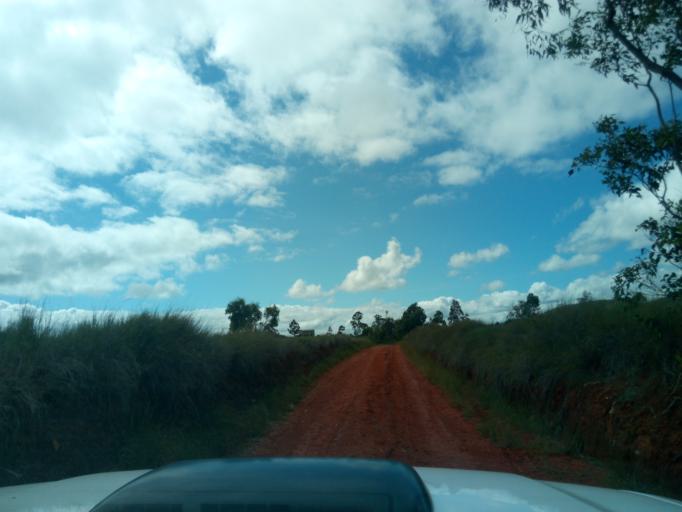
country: MG
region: Analamanga
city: Antananarivo
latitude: -18.7296
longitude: 47.4121
